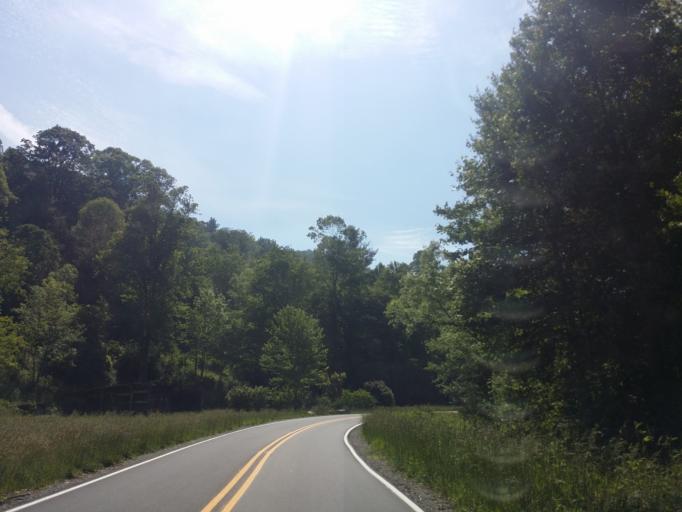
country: US
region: North Carolina
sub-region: Madison County
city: Marshall
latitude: 35.7488
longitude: -82.8630
